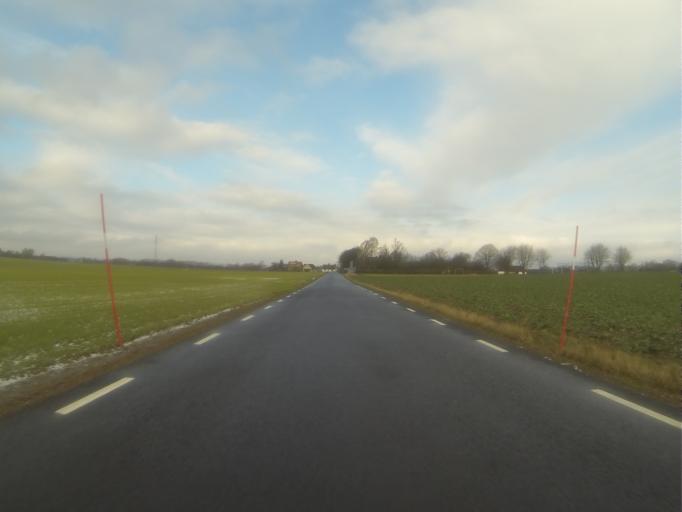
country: SE
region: Skane
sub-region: Svedala Kommun
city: Klagerup
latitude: 55.6216
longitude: 13.3098
